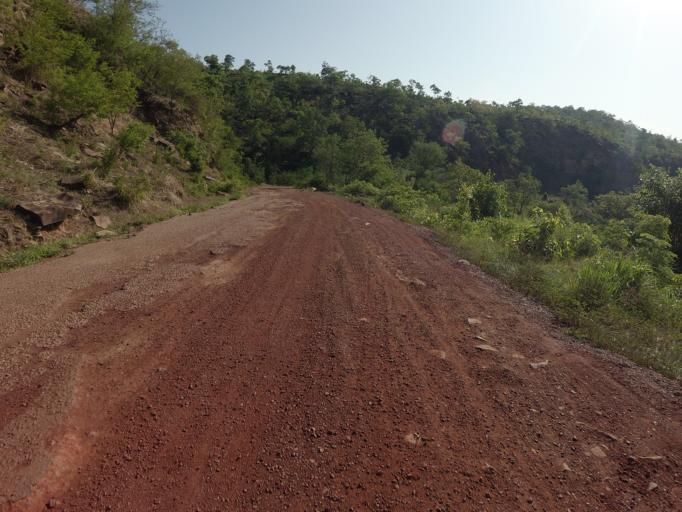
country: GH
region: Upper East
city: Bawku
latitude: 10.6418
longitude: -0.1935
